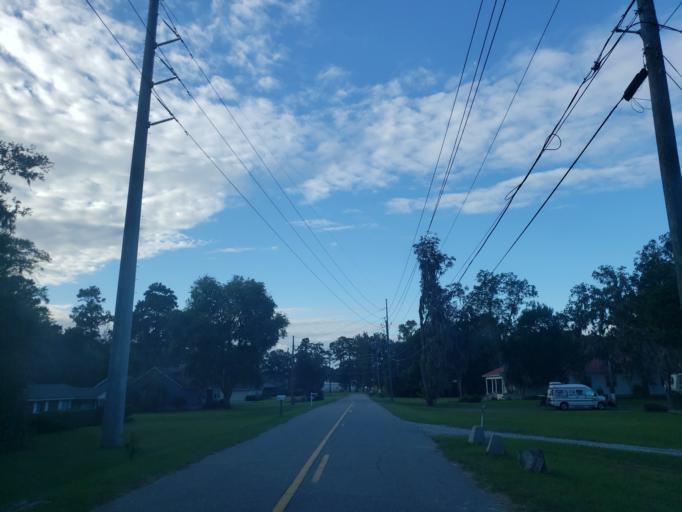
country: US
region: Georgia
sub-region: Chatham County
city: Georgetown
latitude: 31.9878
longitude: -81.2252
